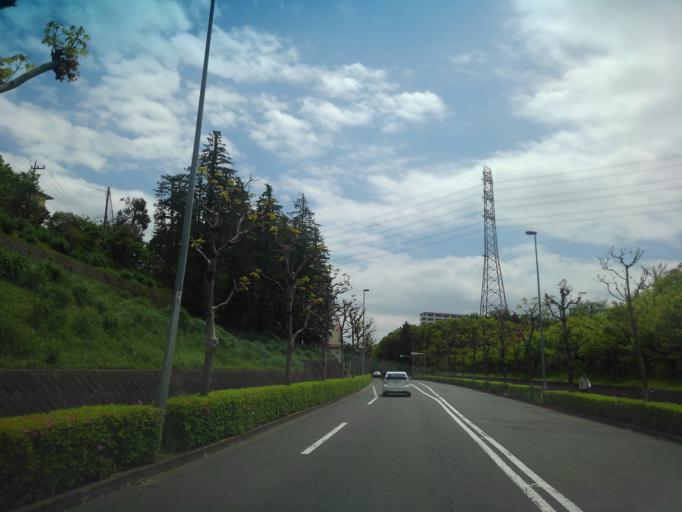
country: JP
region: Tokyo
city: Hino
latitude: 35.6241
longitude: 139.4499
